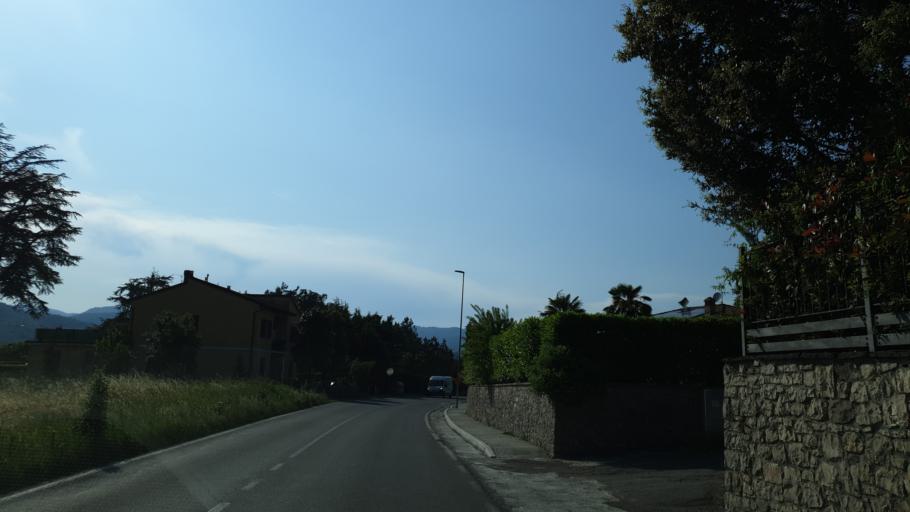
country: IT
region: Tuscany
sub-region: Province of Arezzo
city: Ponte a Poppi
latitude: 43.7360
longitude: 11.7555
